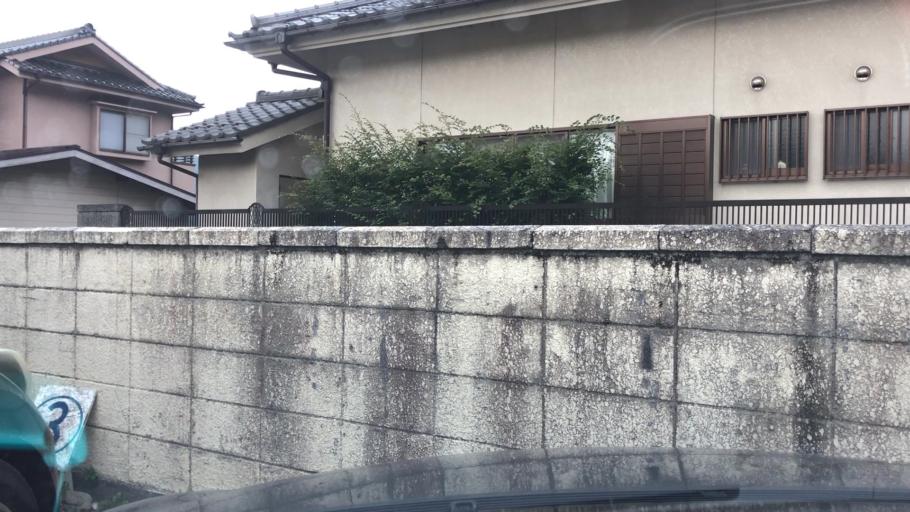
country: JP
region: Tokyo
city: Ome
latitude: 35.8006
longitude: 139.2112
